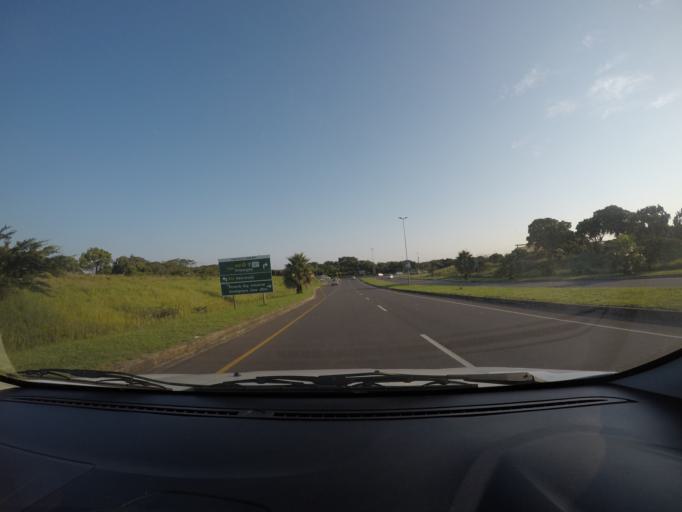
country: ZA
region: KwaZulu-Natal
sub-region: uThungulu District Municipality
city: Richards Bay
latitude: -28.7667
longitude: 32.0486
